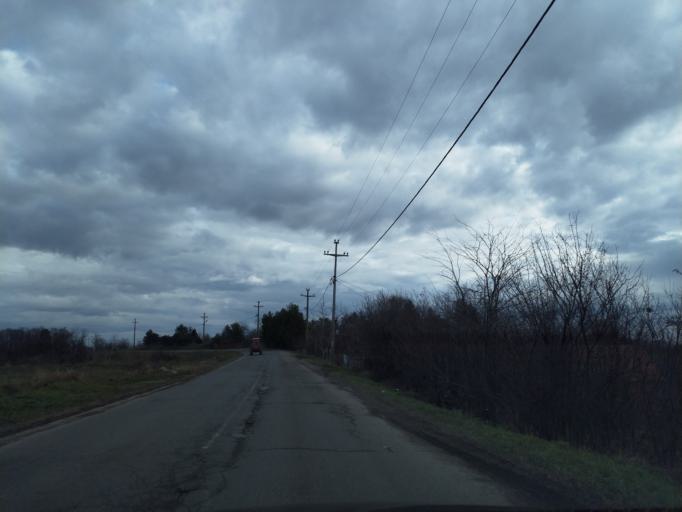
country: RS
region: Central Serbia
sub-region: Belgrade
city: Grocka
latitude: 44.6202
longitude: 20.7398
